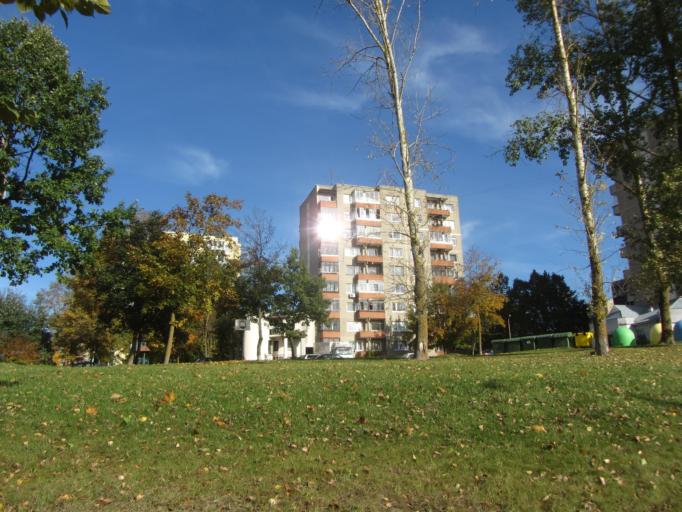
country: LT
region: Vilnius County
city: Elektrenai
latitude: 54.7858
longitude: 24.6732
